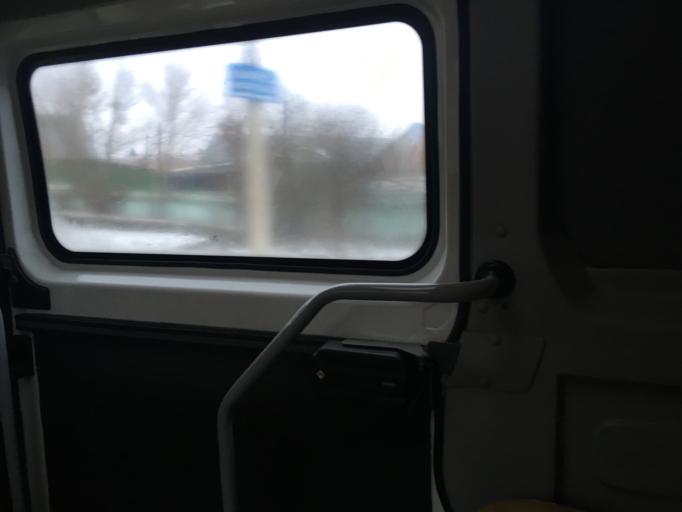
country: RU
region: Tula
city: Dubna
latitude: 54.1071
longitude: 37.1137
